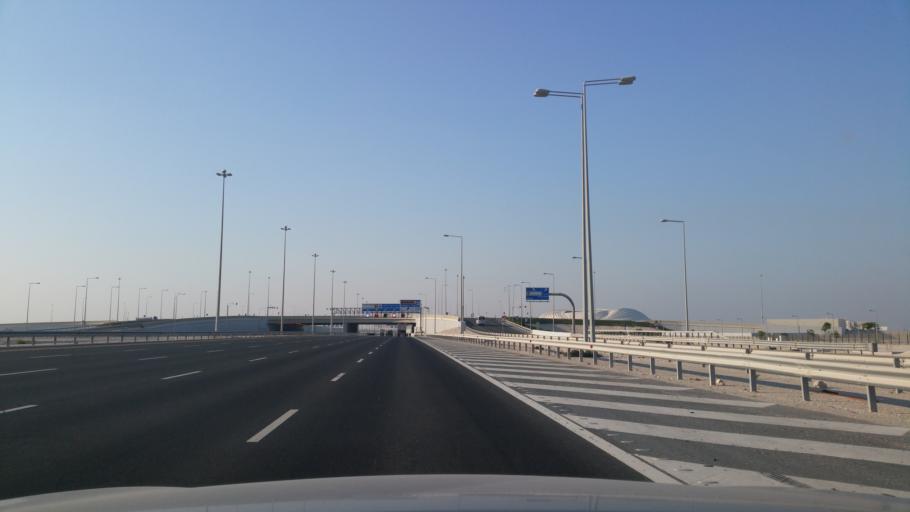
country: QA
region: Al Wakrah
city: Al Wakrah
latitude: 25.1457
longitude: 51.5762
